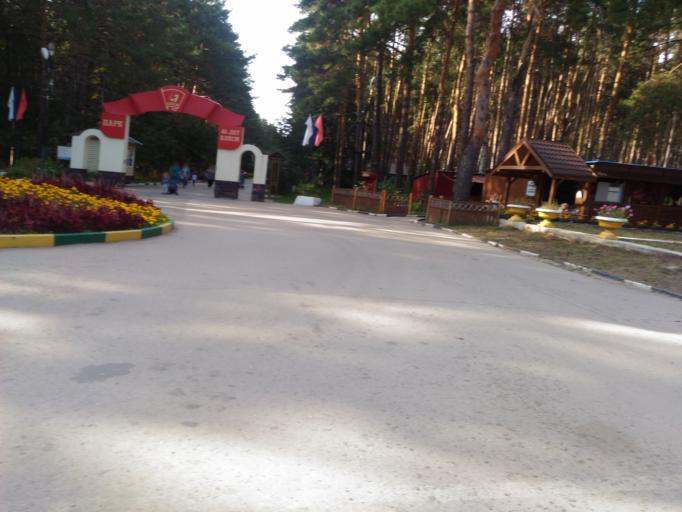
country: RU
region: Ulyanovsk
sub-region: Ulyanovskiy Rayon
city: Ulyanovsk
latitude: 54.3534
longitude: 48.5249
